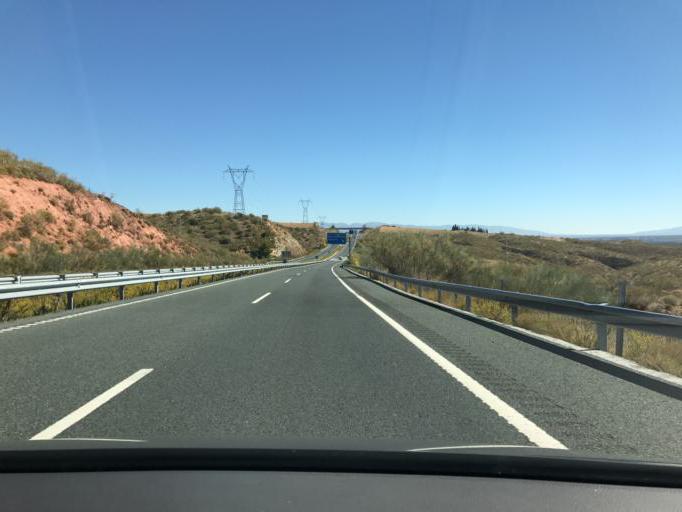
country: ES
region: Andalusia
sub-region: Provincia de Granada
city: Diezma
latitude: 37.3151
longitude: -3.3459
